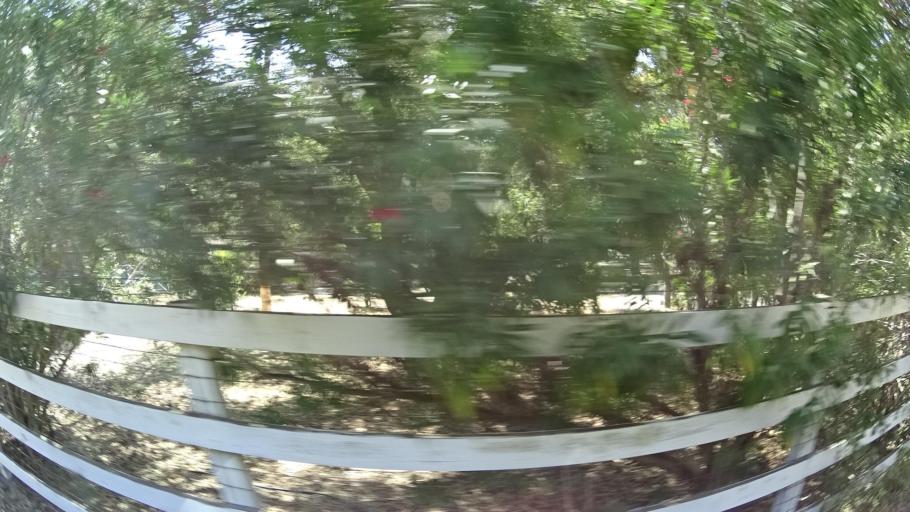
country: US
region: California
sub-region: San Diego County
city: Fallbrook
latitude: 33.4559
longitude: -117.2986
